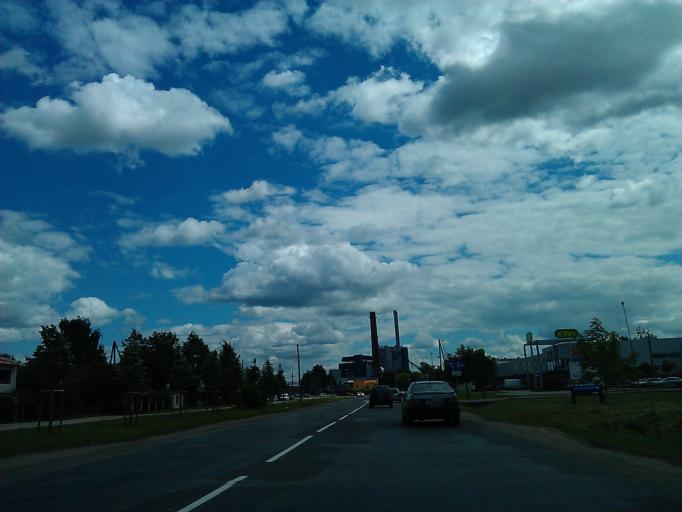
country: LV
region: Jelgava
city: Jelgava
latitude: 56.6381
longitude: 23.7032
